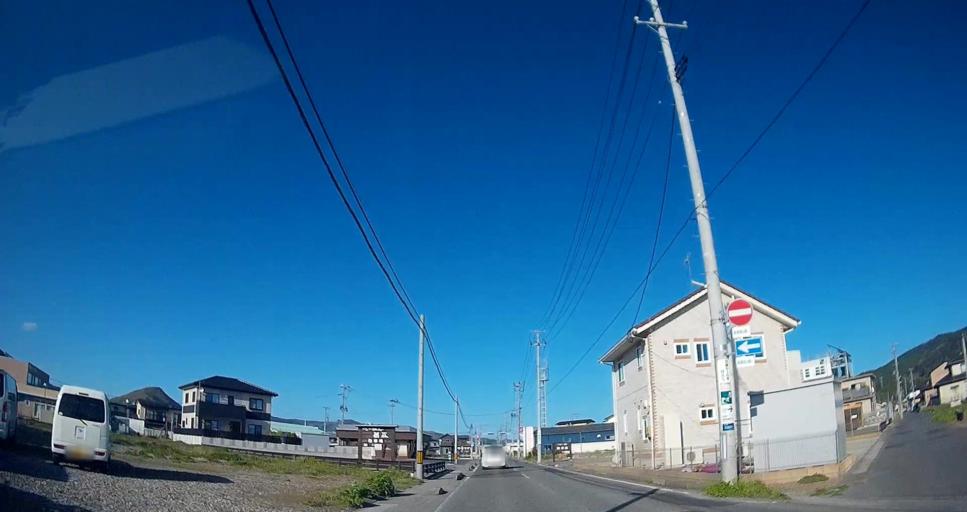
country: JP
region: Miyagi
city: Ishinomaki
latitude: 38.4164
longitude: 141.3615
